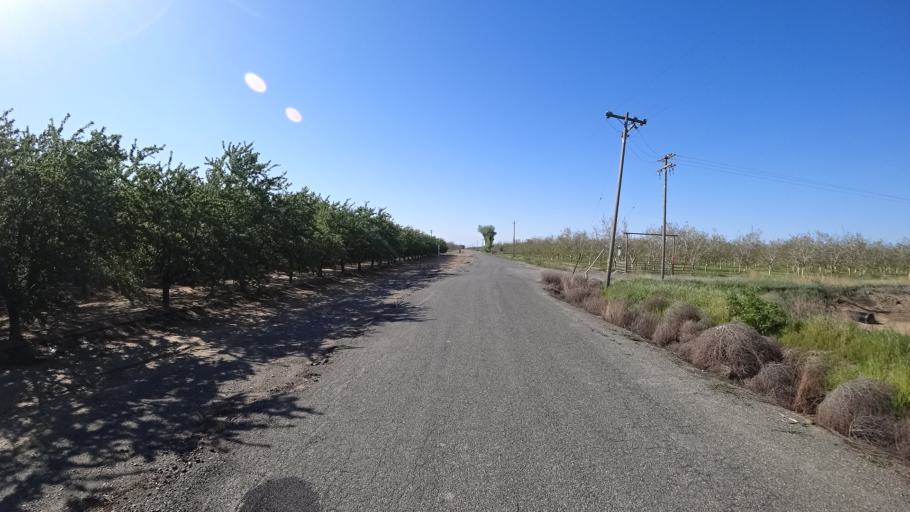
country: US
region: California
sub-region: Glenn County
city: Hamilton City
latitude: 39.6963
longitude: -122.0742
